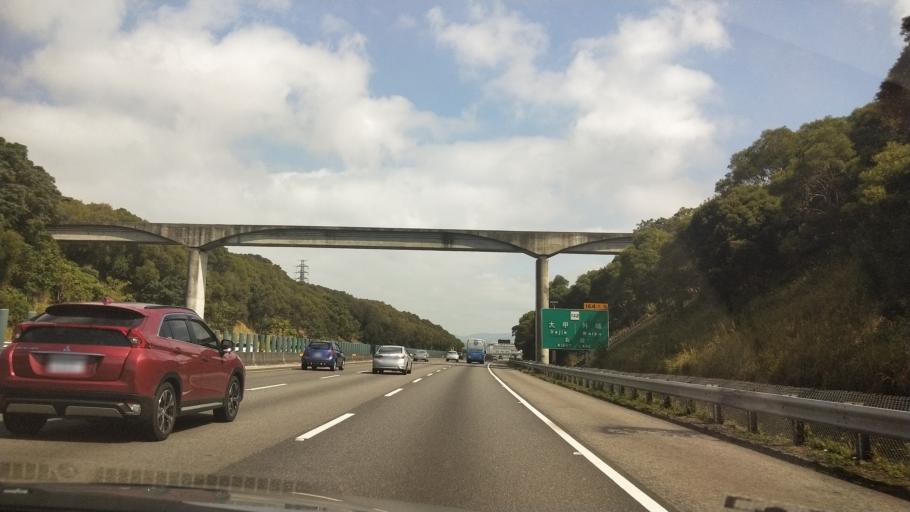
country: TW
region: Taiwan
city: Fengyuan
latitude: 24.3308
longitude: 120.6291
